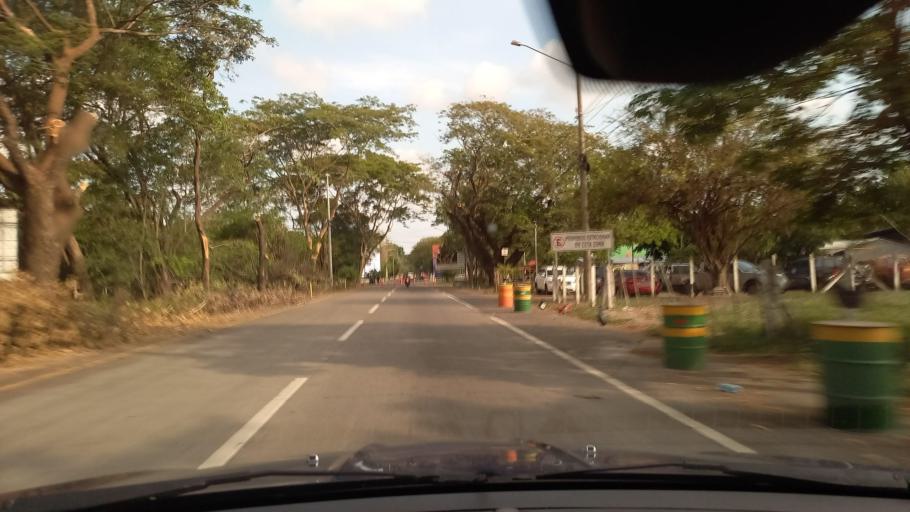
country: SV
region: La Paz
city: El Rosario
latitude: 13.4567
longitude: -89.0617
